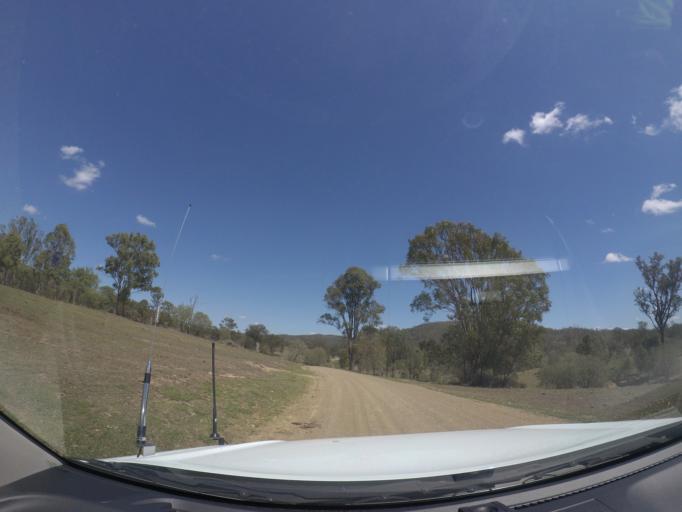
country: AU
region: Queensland
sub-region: Logan
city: Cedar Vale
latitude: -27.8575
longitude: 152.8713
